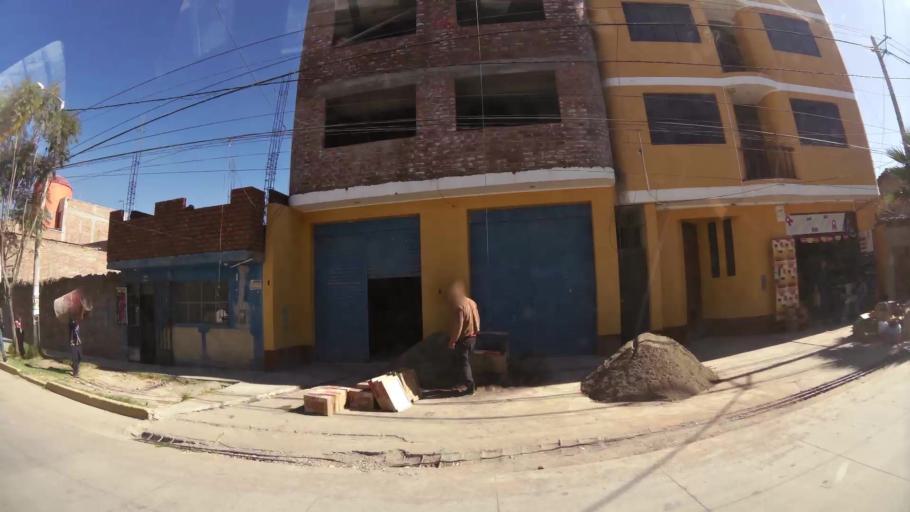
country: PE
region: Ayacucho
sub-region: Provincia de Huamanga
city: Ayacucho
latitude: -13.1618
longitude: -74.2146
